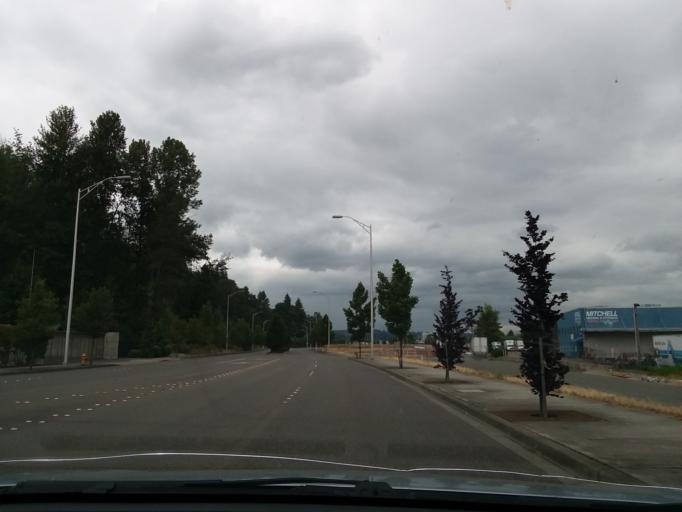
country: US
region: Washington
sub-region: King County
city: SeaTac
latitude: 47.4328
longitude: -122.2651
